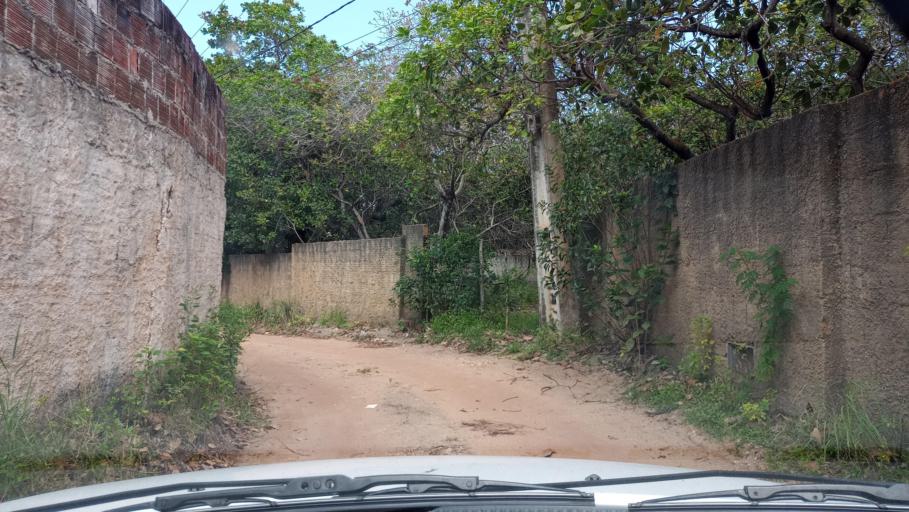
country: BR
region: Rio Grande do Norte
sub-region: Ares
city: Ares
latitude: -6.2408
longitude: -35.0451
